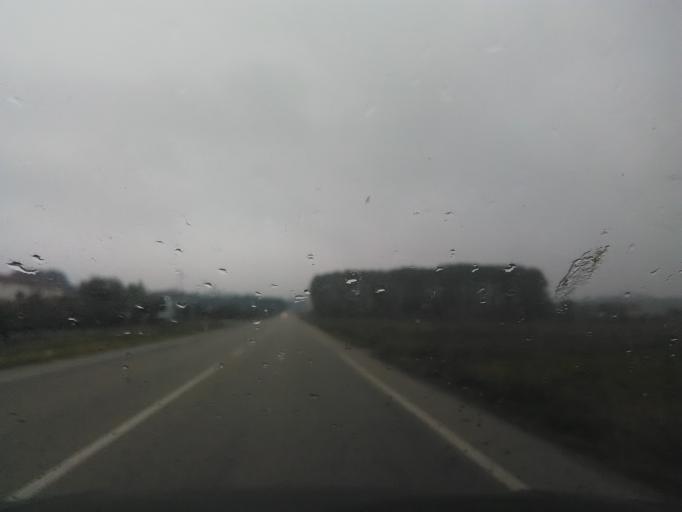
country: IT
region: Piedmont
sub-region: Provincia di Biella
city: Cavaglia
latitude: 45.4032
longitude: 8.1061
